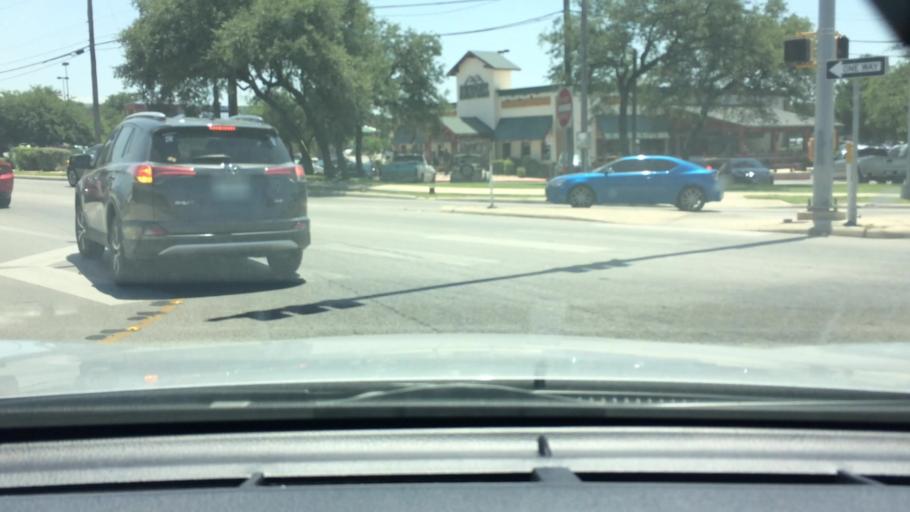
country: US
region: Texas
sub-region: Bexar County
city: Shavano Park
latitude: 29.5631
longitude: -98.5915
